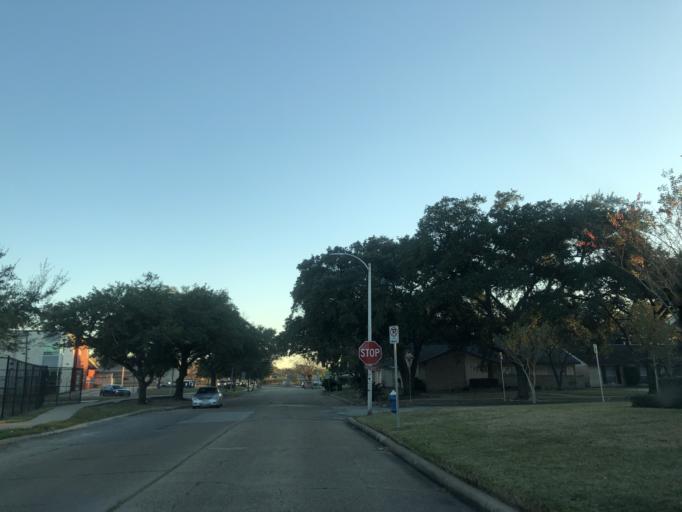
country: US
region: Texas
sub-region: Harris County
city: Bellaire
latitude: 29.6887
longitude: -95.5138
